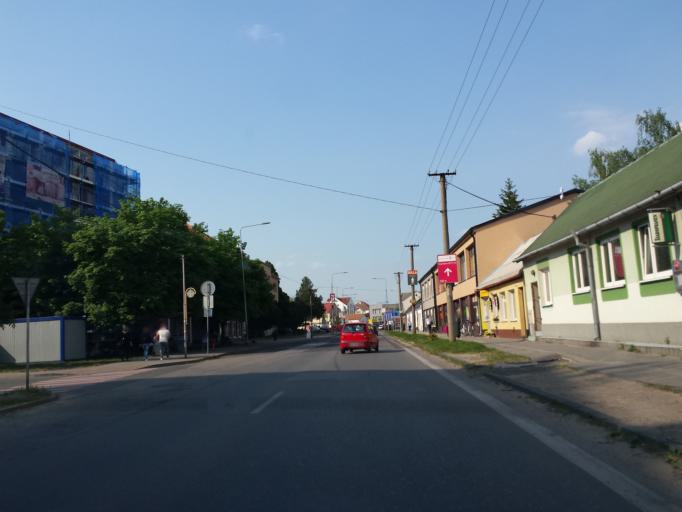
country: SK
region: Bratislavsky
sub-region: Okres Malacky
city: Malacky
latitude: 48.4350
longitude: 17.0176
